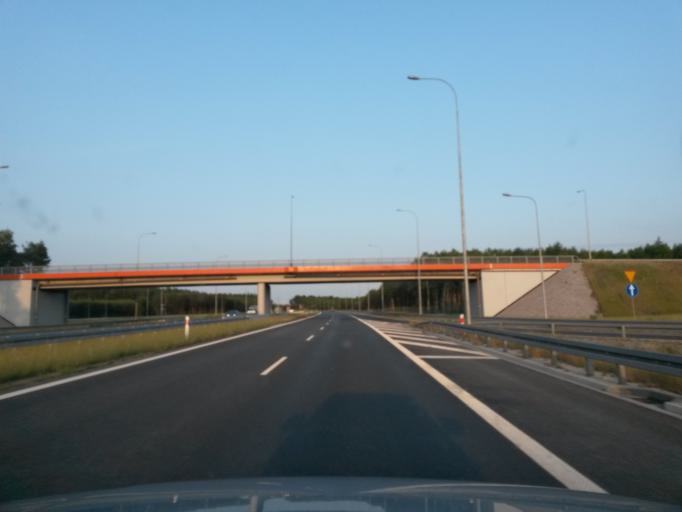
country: PL
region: Lodz Voivodeship
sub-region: Powiat wieruszowski
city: Wieruszow
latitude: 51.3080
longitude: 18.1851
